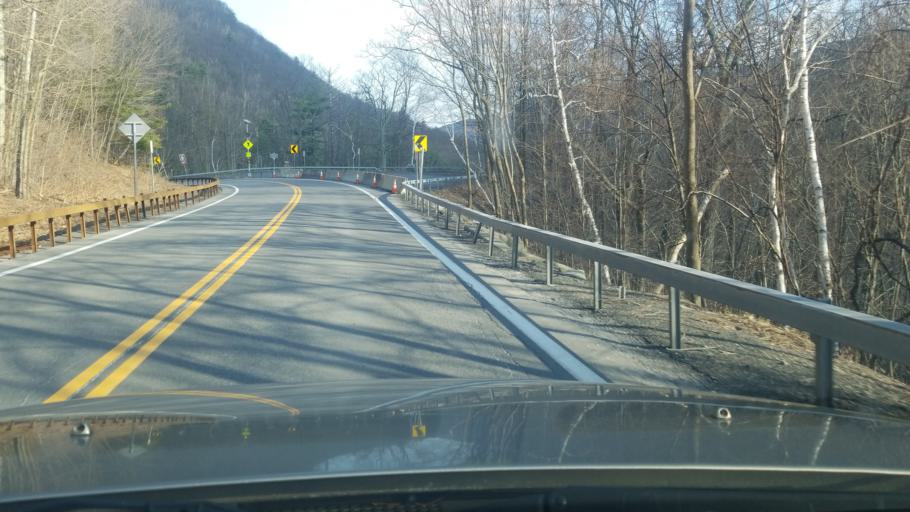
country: US
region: New York
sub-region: Greene County
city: Palenville
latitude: 42.1902
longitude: -74.0749
